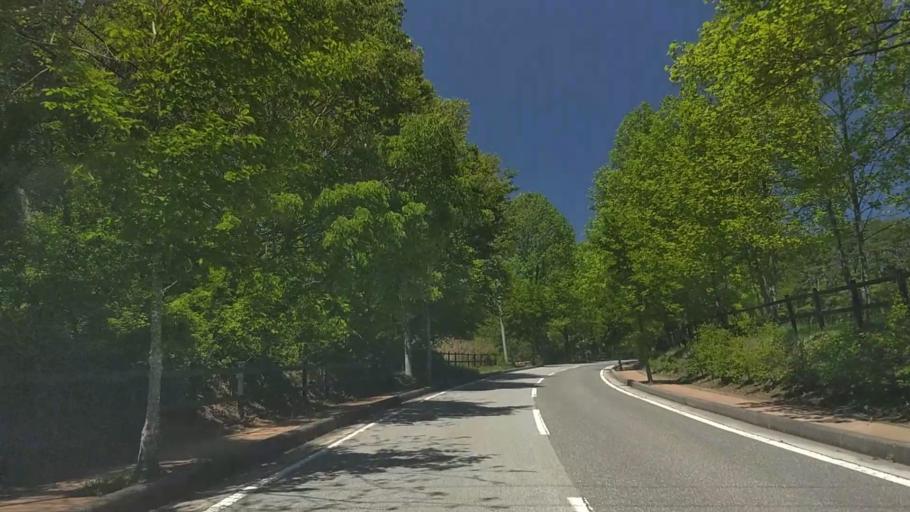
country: JP
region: Yamanashi
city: Nirasaki
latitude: 35.8943
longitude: 138.4393
